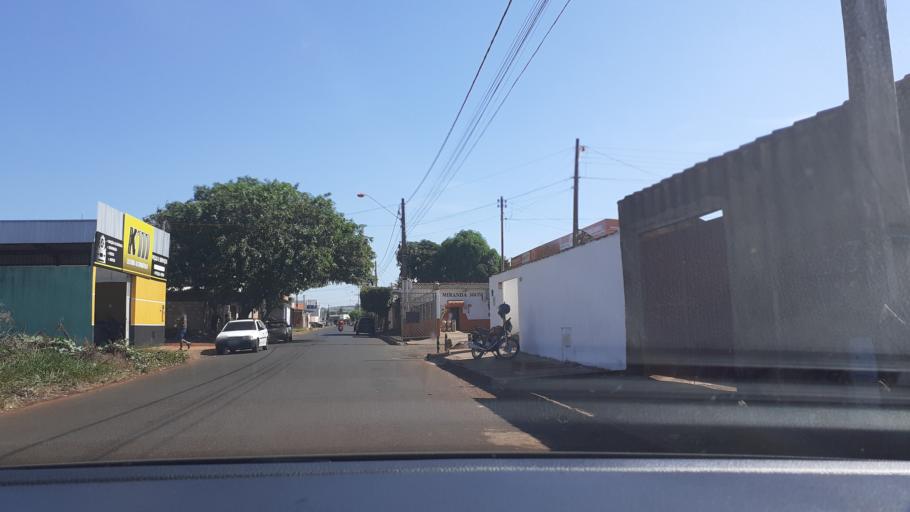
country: BR
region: Goias
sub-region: Itumbiara
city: Itumbiara
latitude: -18.4148
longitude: -49.2516
